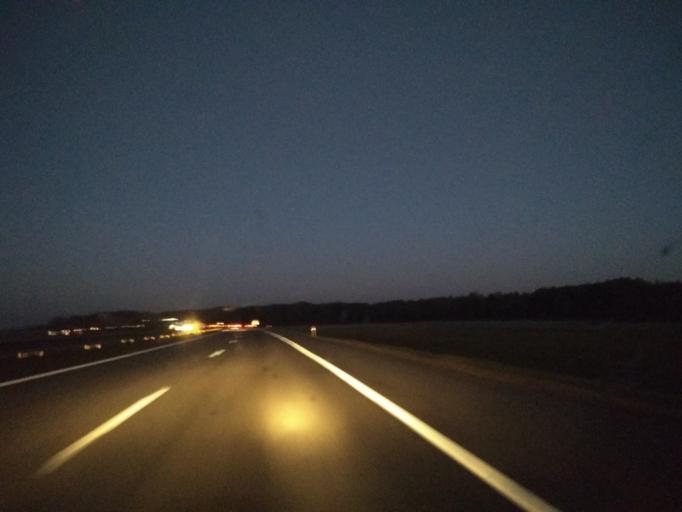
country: BY
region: Minsk
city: Dzyarzhynsk
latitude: 53.6598
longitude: 27.1275
